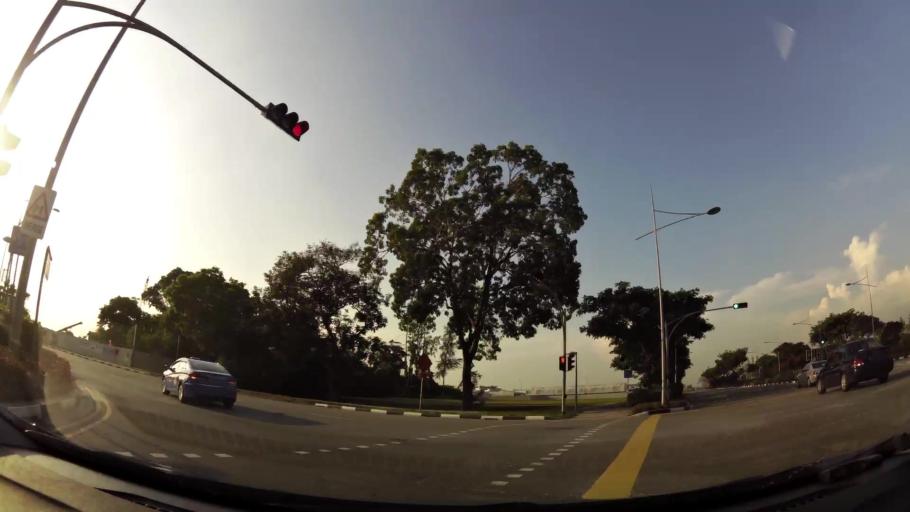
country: SG
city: Singapore
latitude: 1.2757
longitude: 103.8621
